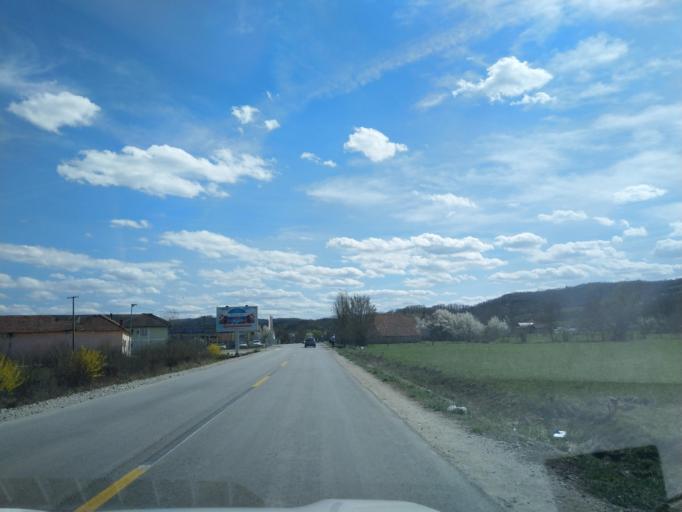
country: RS
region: Central Serbia
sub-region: Zlatiborski Okrug
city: Arilje
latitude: 43.7980
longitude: 20.0972
